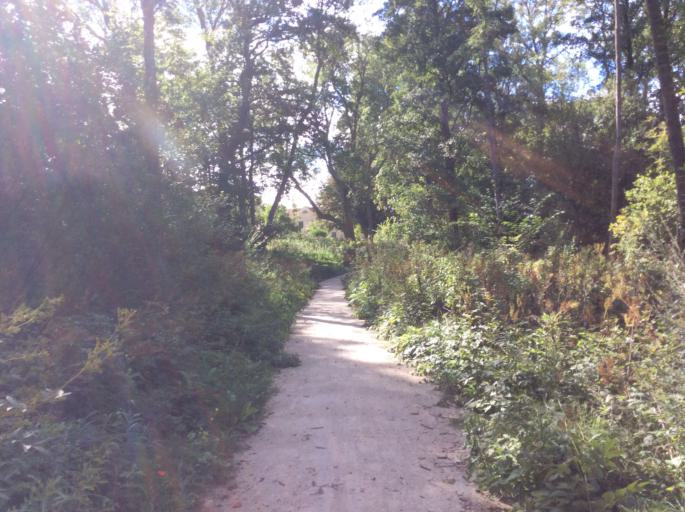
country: SE
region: Gotland
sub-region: Gotland
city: Visby
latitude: 57.6205
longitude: 18.2746
